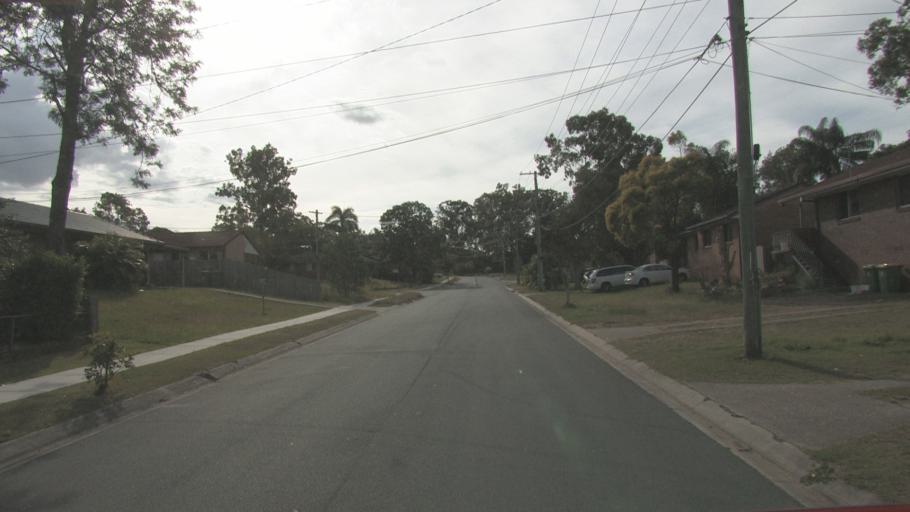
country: AU
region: Queensland
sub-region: Logan
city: Logan City
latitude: -27.6624
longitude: 153.1034
